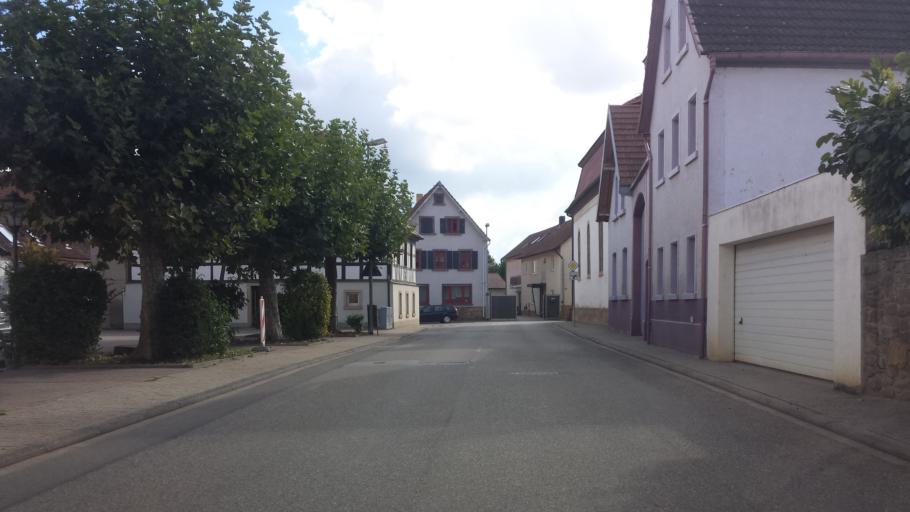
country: DE
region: Rheinland-Pfalz
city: Hochdorf-Assenheim
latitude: 49.4249
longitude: 8.2854
